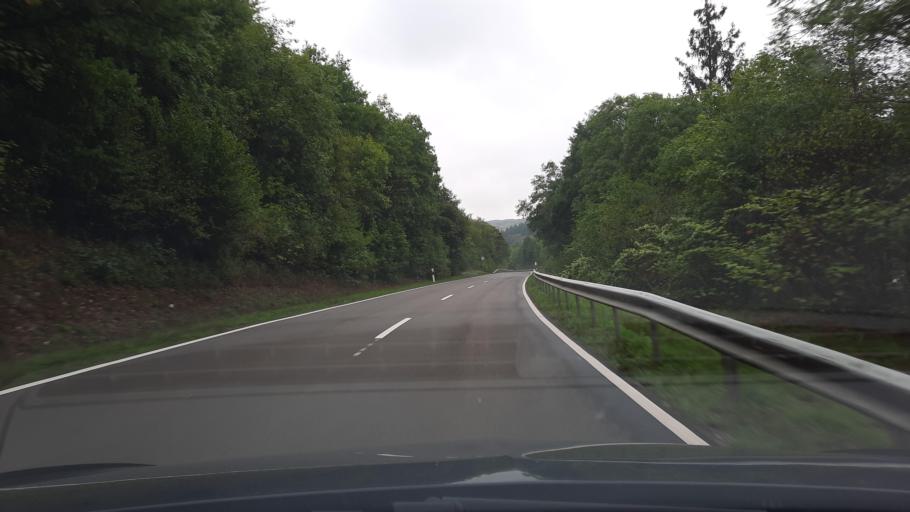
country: DE
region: Rheinland-Pfalz
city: Morscheid
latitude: 49.7334
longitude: 6.7394
